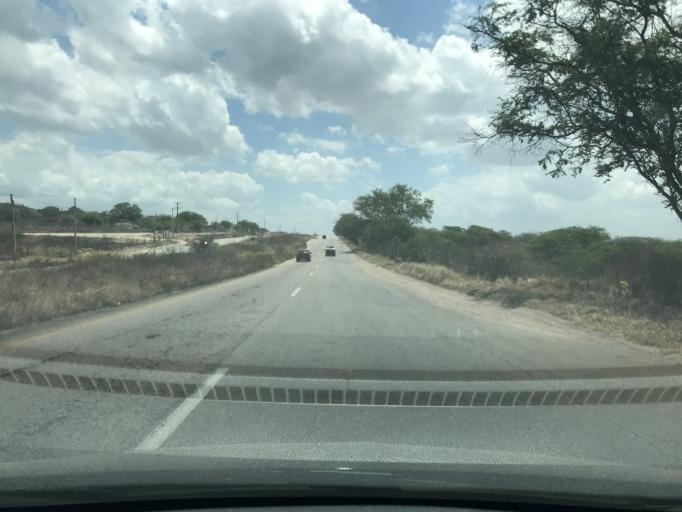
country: BR
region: Pernambuco
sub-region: Caruaru
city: Caruaru
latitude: -8.2949
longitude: -35.8872
